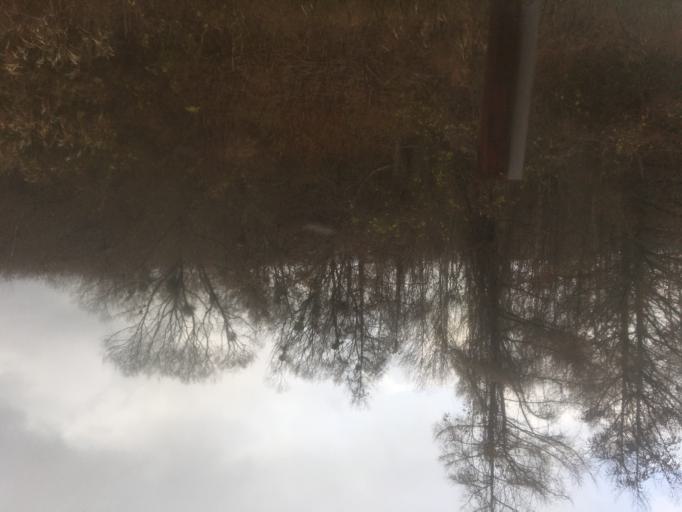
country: JP
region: Aomori
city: Goshogawara
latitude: 41.1811
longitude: 140.4890
